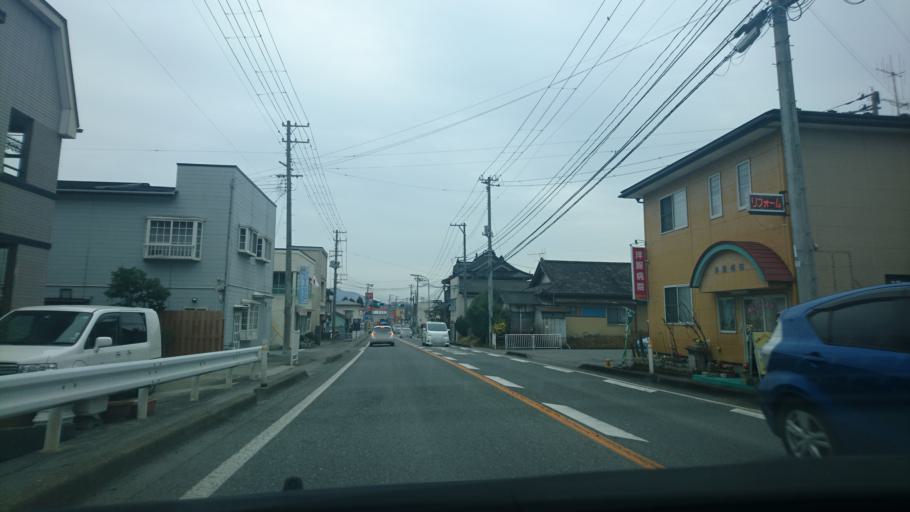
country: JP
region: Iwate
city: Ofunato
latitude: 39.0734
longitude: 141.7133
